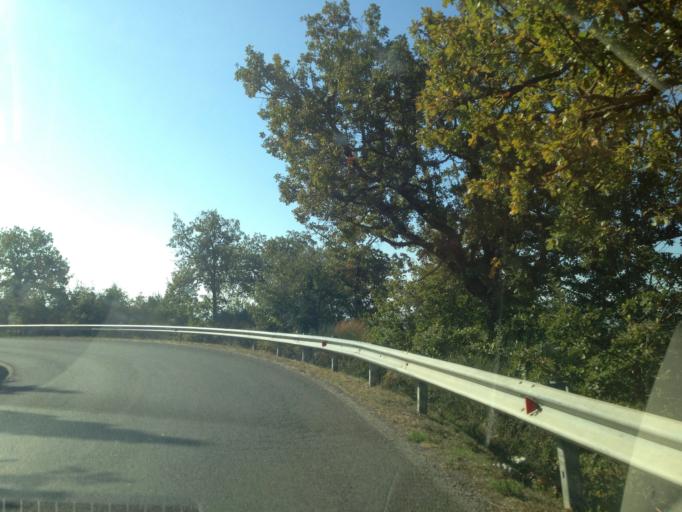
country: IT
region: Tuscany
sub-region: Provincia di Siena
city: Castellina in Chianti
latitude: 43.4442
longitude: 11.2993
